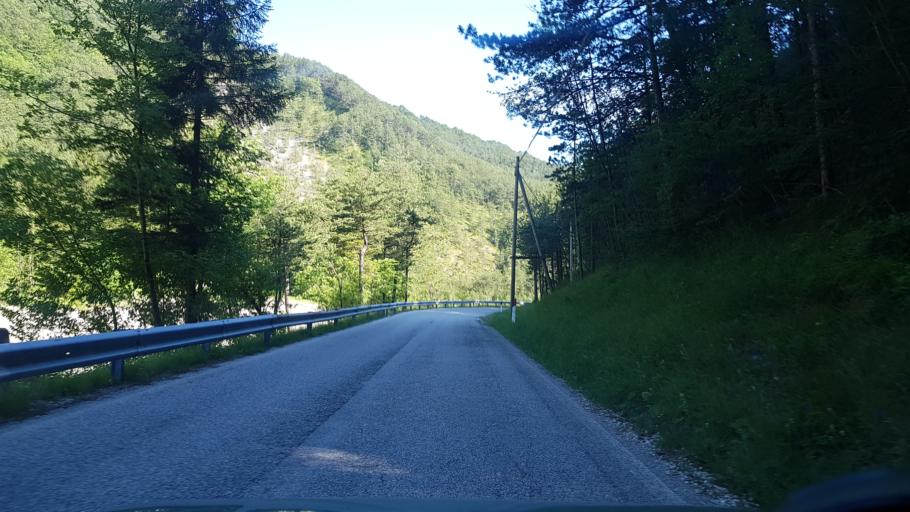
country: IT
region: Friuli Venezia Giulia
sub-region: Provincia di Udine
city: Moggio Udinese
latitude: 46.4571
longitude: 13.1904
